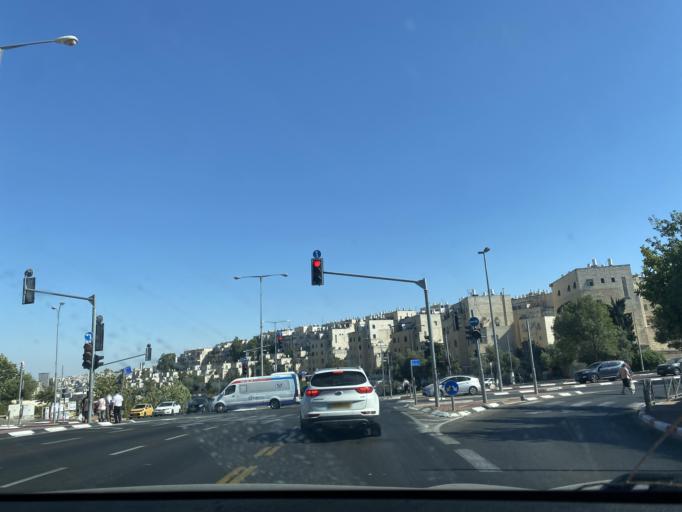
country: PS
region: West Bank
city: Bayt Iksa
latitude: 31.8221
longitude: 35.1893
